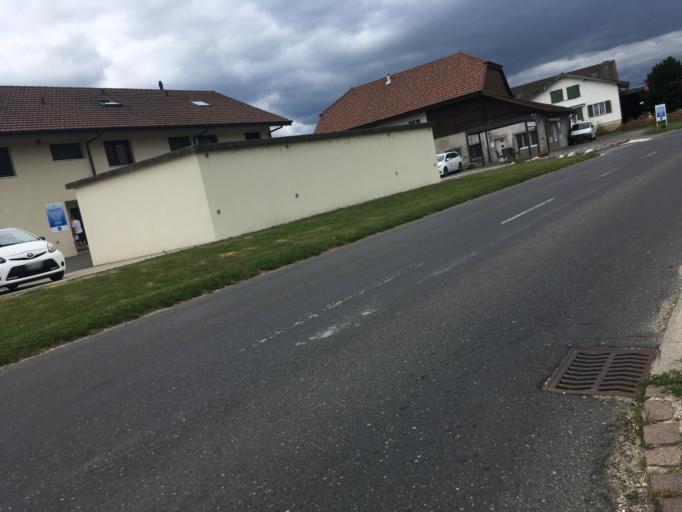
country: CH
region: Vaud
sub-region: Broye-Vully District
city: Payerne
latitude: 46.8736
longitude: 6.9273
